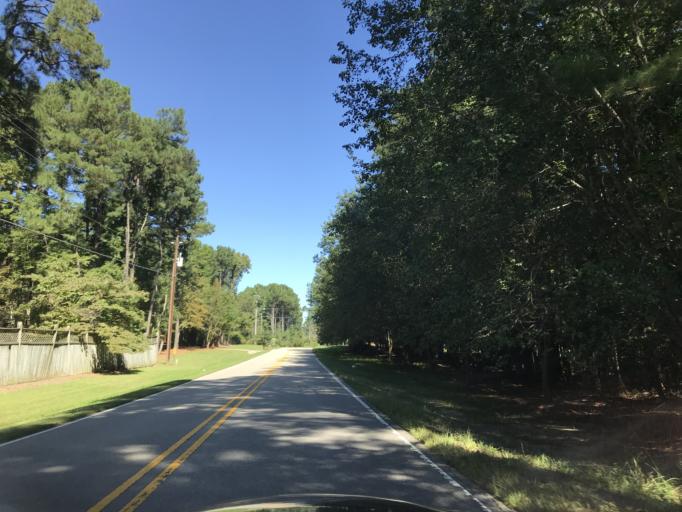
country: US
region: North Carolina
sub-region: Wake County
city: Wake Forest
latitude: 35.9539
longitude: -78.6250
